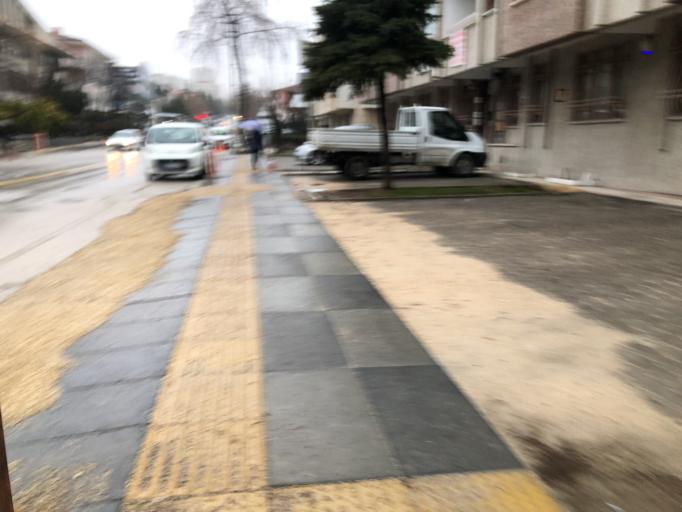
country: TR
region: Ankara
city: Ankara
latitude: 39.8930
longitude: 32.8269
